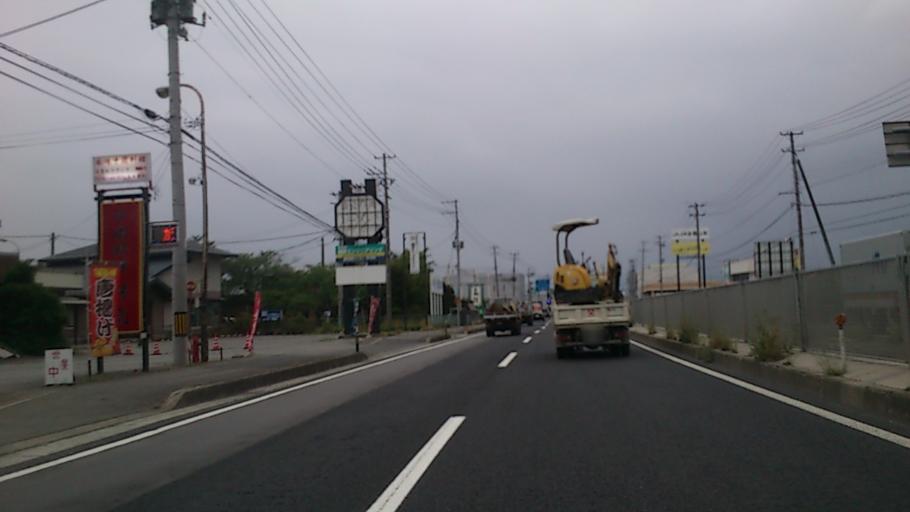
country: JP
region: Yamagata
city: Tendo
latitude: 38.3343
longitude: 140.3703
